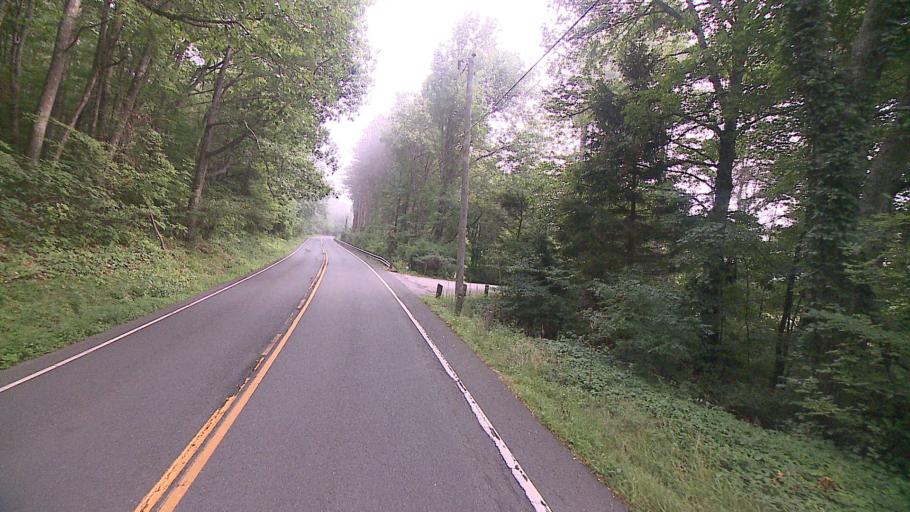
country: US
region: Connecticut
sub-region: Litchfield County
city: Canaan
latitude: 41.9200
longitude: -73.3651
